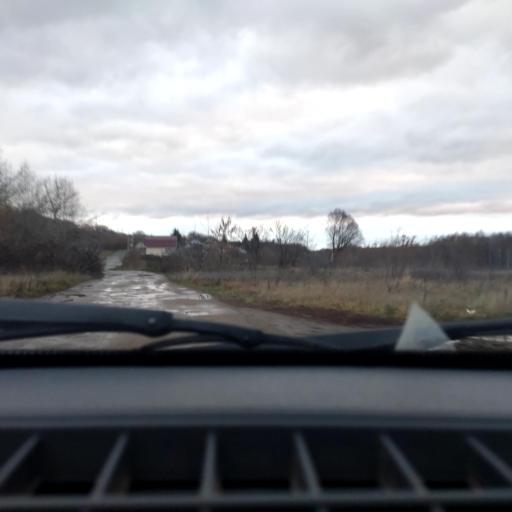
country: RU
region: Bashkortostan
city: Avdon
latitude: 54.6376
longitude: 55.7283
